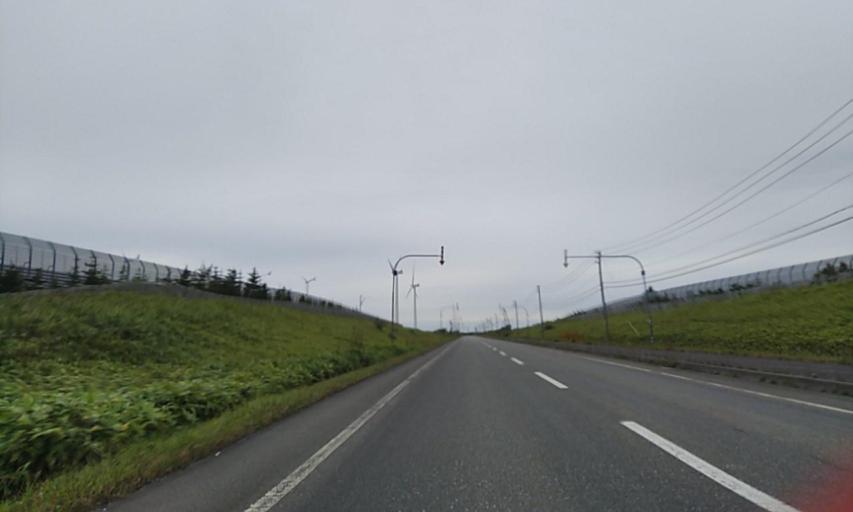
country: JP
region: Hokkaido
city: Makubetsu
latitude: 45.2884
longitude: 142.2156
